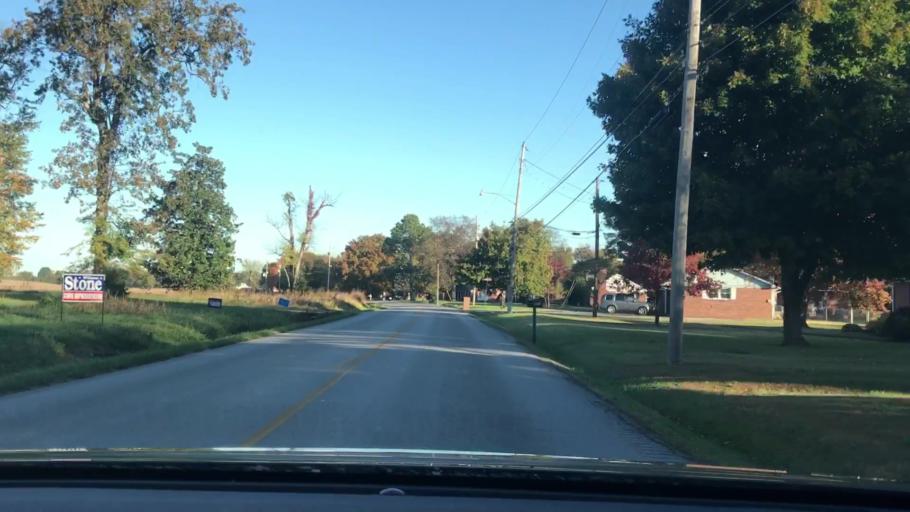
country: US
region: Kentucky
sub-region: Simpson County
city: Franklin
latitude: 36.7372
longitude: -86.5844
